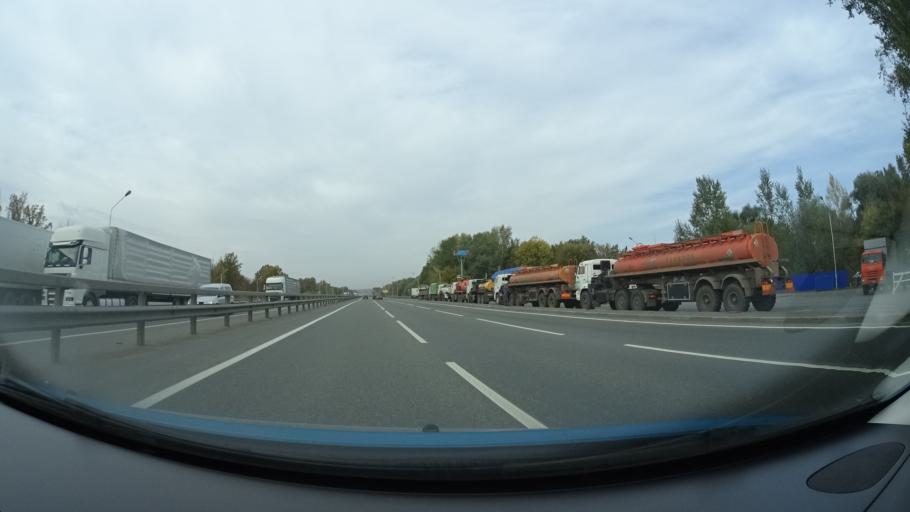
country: RU
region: Bashkortostan
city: Ufa
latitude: 54.6643
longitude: 55.8647
